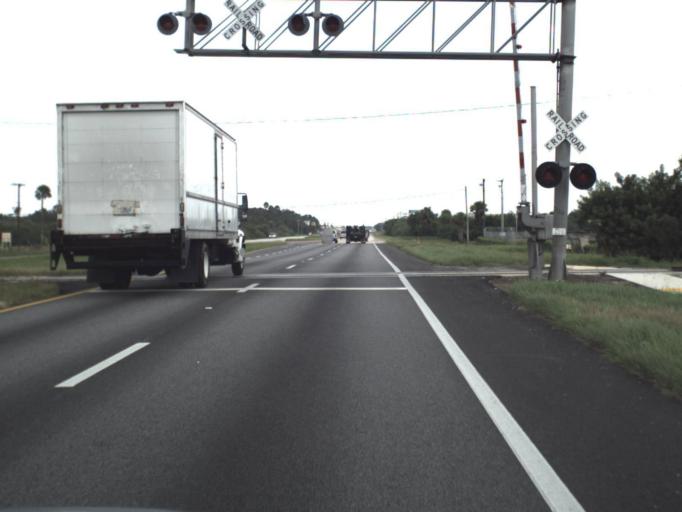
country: US
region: Florida
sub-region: Hillsborough County
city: Palm River-Clair Mel
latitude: 27.9520
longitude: -82.3978
